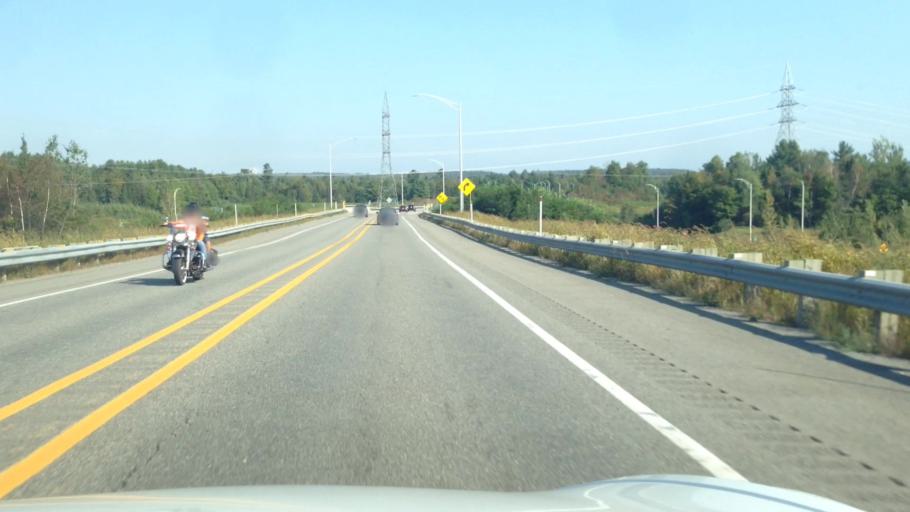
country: CA
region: Ontario
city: Clarence-Rockland
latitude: 45.6055
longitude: -75.3877
